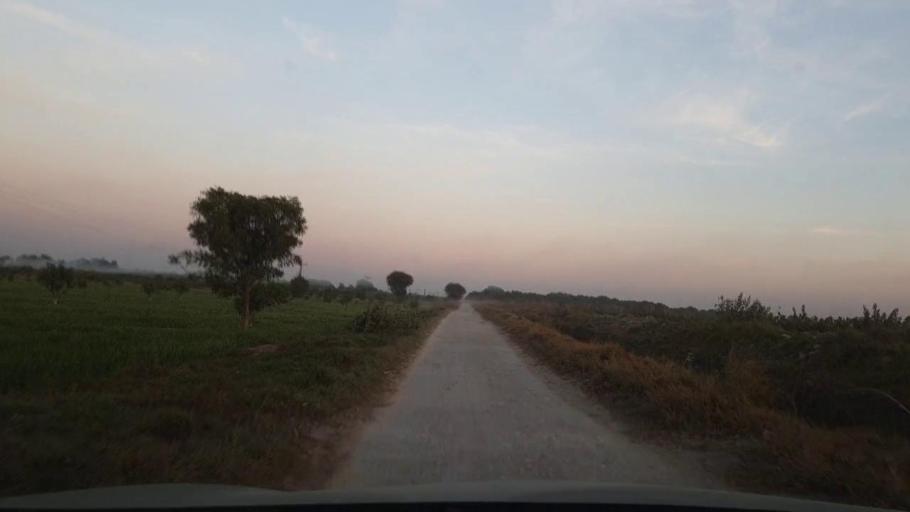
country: PK
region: Sindh
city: Tando Allahyar
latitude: 25.5632
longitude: 68.7658
